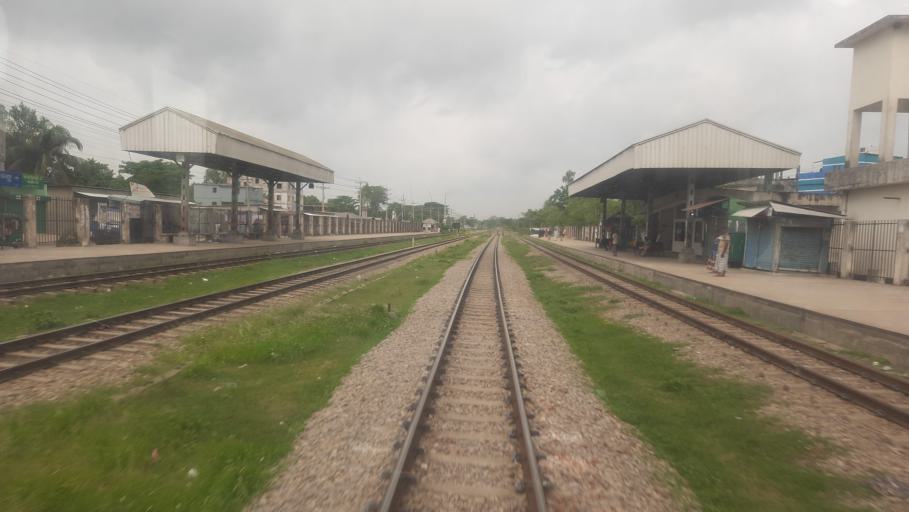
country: BD
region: Dhaka
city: Narsingdi
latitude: 23.9356
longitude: 90.7719
